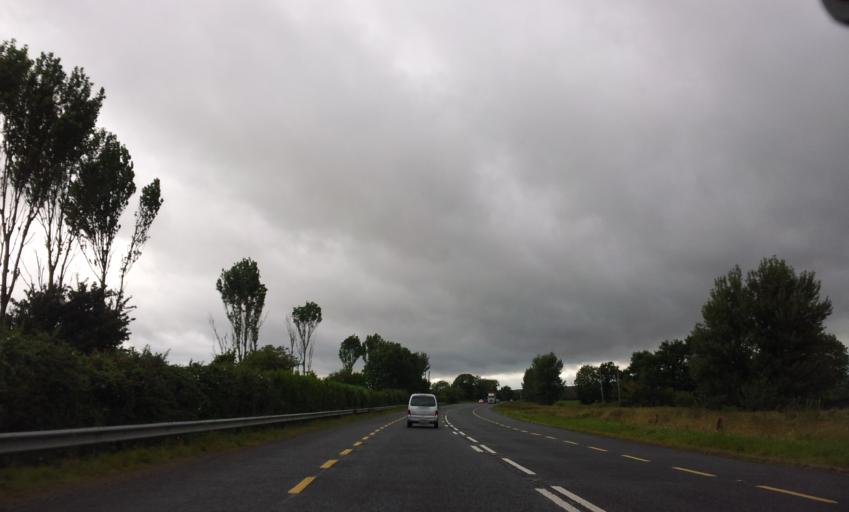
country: IE
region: Munster
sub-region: County Cork
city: Castlemartyr
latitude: 51.9371
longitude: -7.9570
